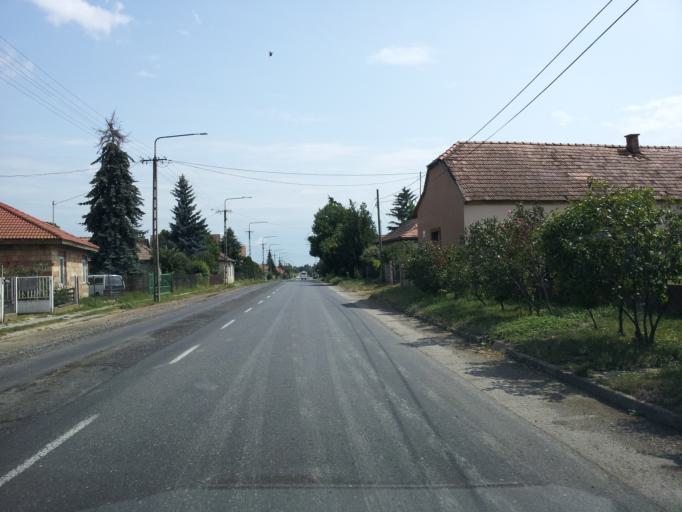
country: HU
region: Fejer
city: Enying
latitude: 46.9499
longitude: 18.2285
